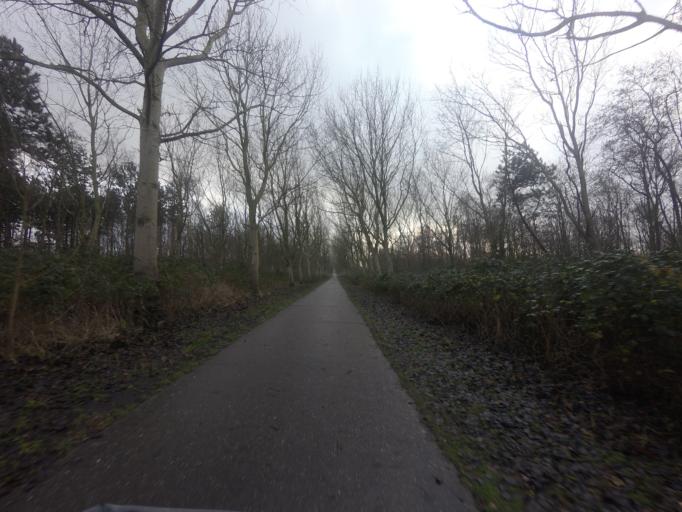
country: NL
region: North Holland
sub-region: Gemeente Texel
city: Den Burg
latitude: 53.1627
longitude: 4.8519
